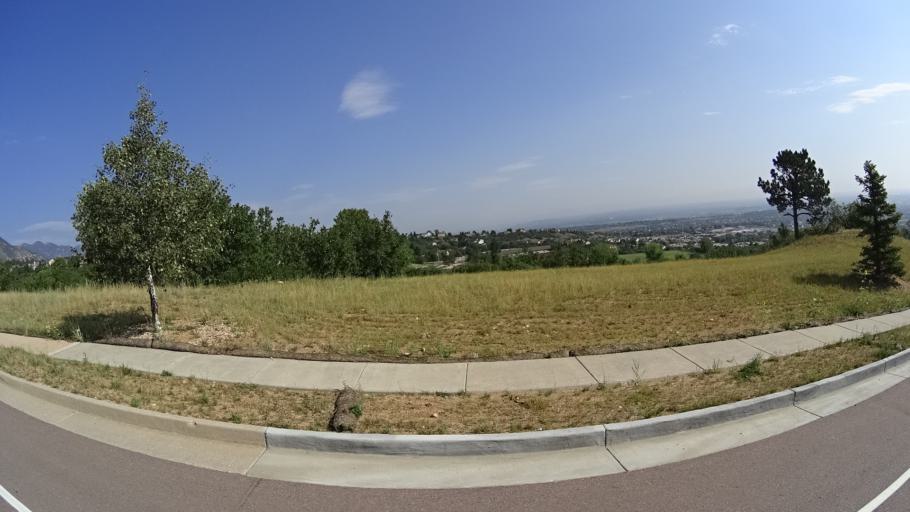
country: US
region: Colorado
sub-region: El Paso County
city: Fort Carson
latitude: 38.7571
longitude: -104.8240
